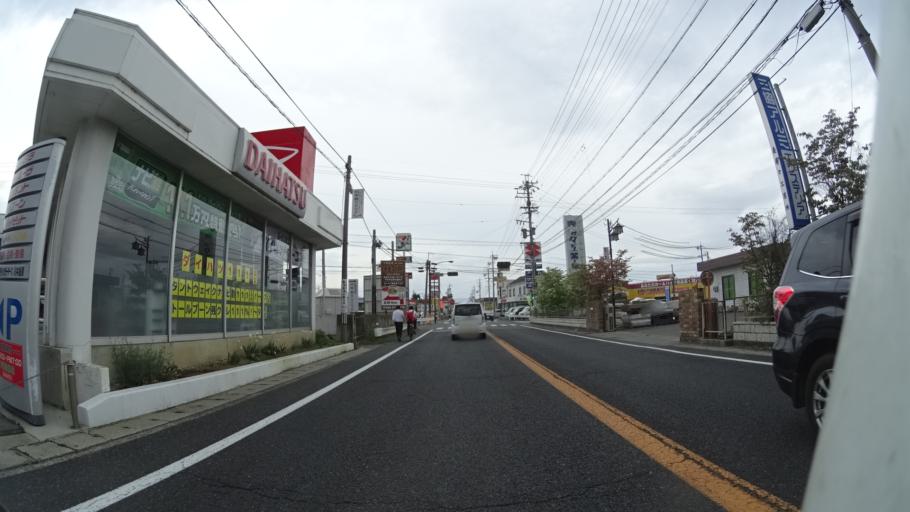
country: JP
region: Nagano
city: Nagano-shi
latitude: 36.5887
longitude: 138.1533
